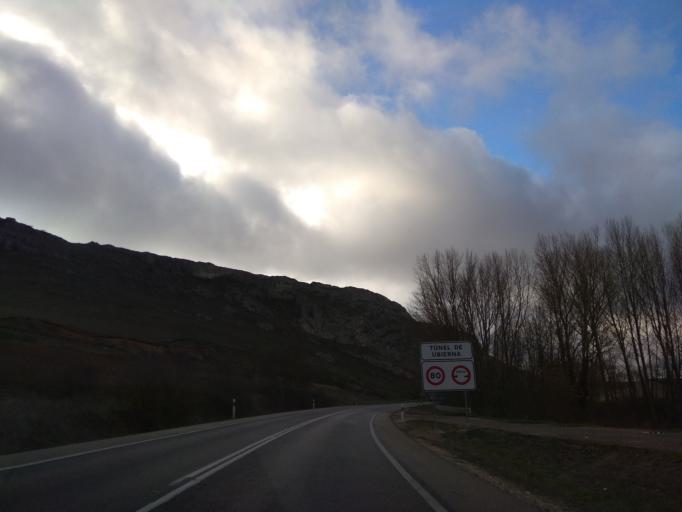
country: ES
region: Castille and Leon
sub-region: Provincia de Burgos
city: Quintanaortuno
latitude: 42.4934
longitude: -3.6952
